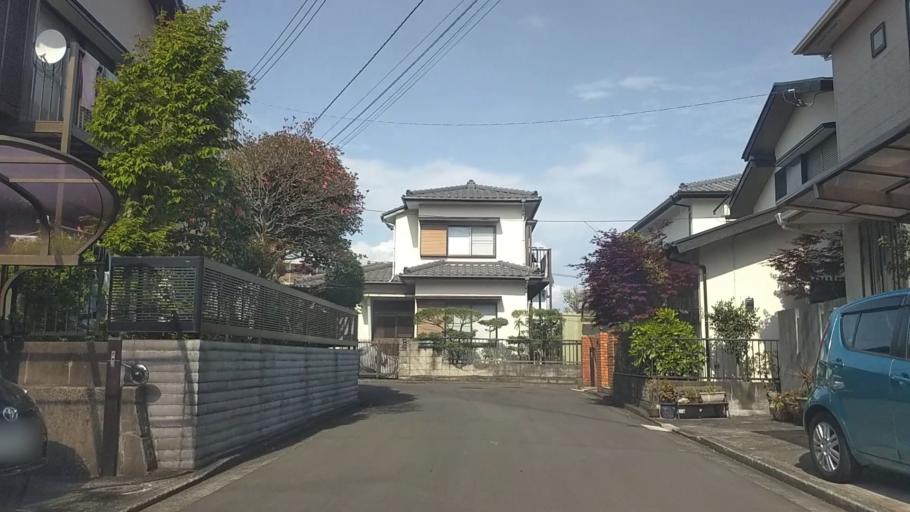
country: JP
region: Kanagawa
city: Kamakura
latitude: 35.3822
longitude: 139.5682
